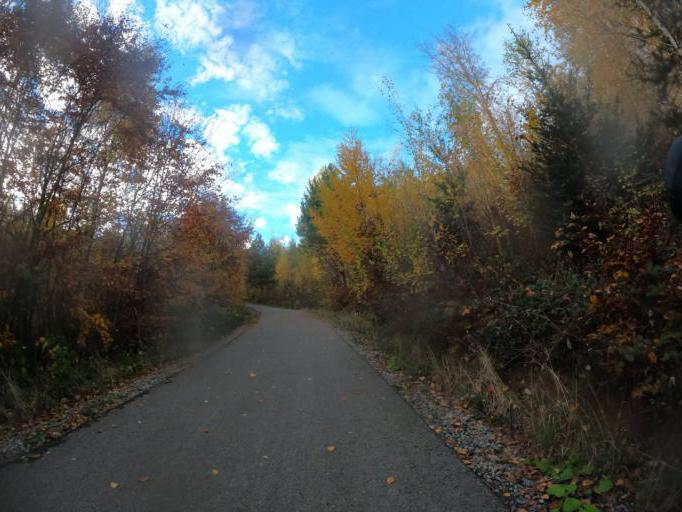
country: DE
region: Baden-Wuerttemberg
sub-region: Regierungsbezirk Stuttgart
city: Sindelfingen
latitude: 48.7179
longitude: 9.0302
